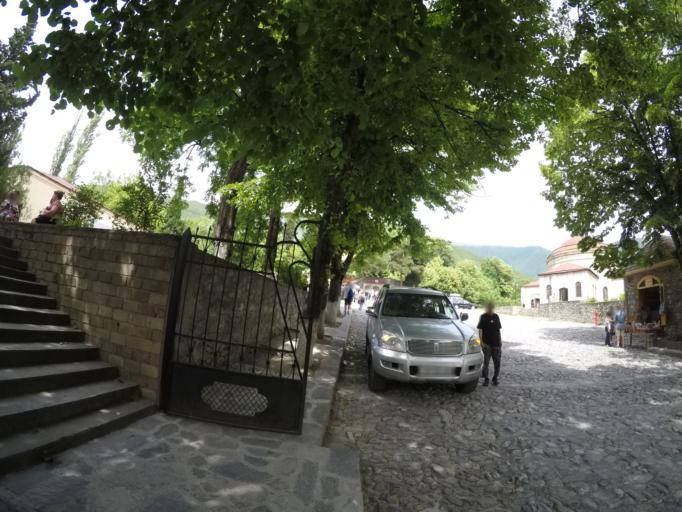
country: AZ
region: Shaki City
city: Sheki
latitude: 41.2033
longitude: 47.1962
